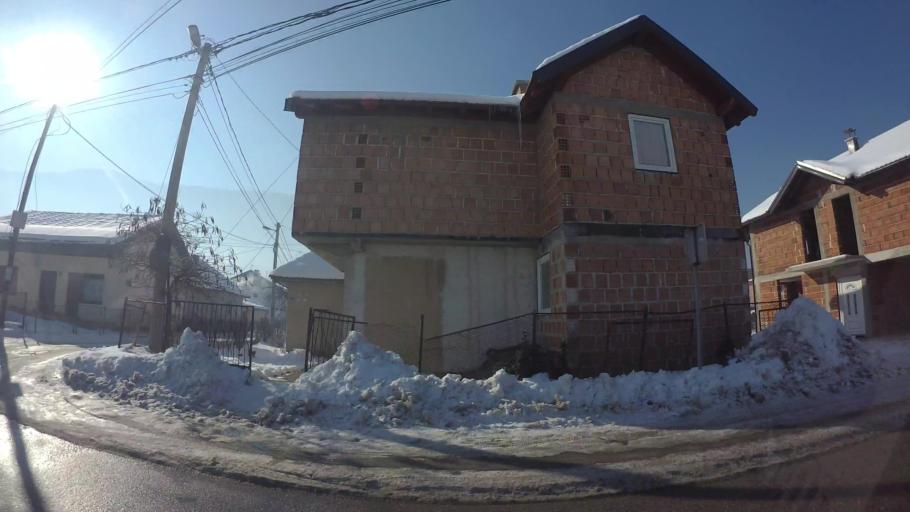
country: BA
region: Federation of Bosnia and Herzegovina
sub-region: Kanton Sarajevo
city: Sarajevo
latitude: 43.8069
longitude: 18.3008
